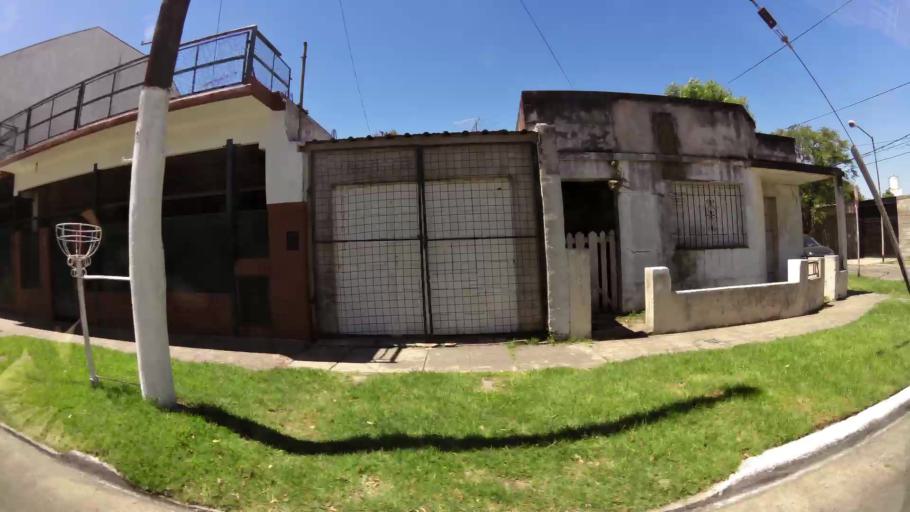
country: AR
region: Buenos Aires
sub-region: Partido de Vicente Lopez
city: Olivos
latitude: -34.5146
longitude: -58.5355
